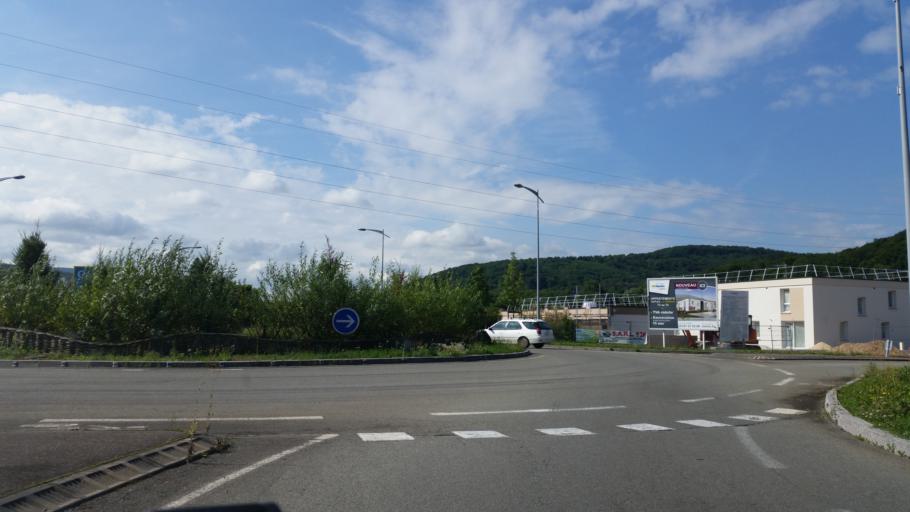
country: FR
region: Franche-Comte
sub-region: Departement du Doubs
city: Mathay
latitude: 47.4284
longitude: 6.7826
